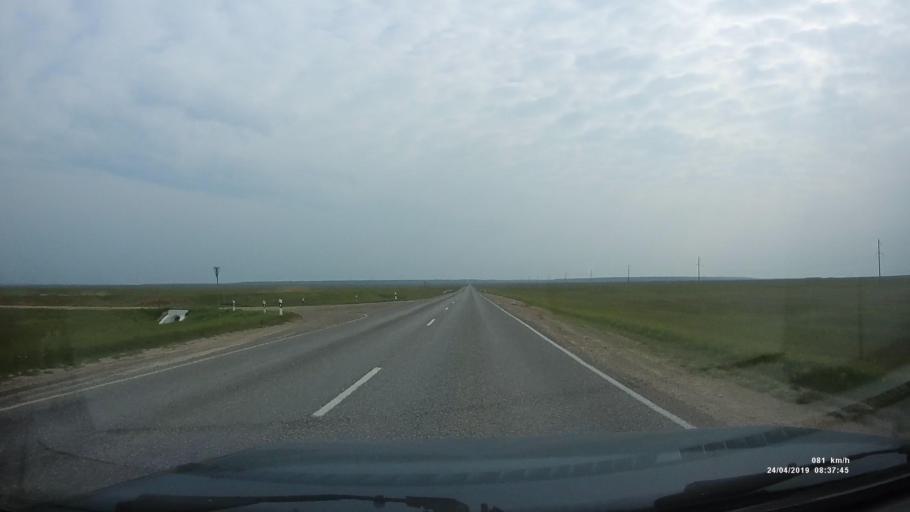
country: RU
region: Kalmykiya
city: Arshan'
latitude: 46.2117
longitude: 43.9560
